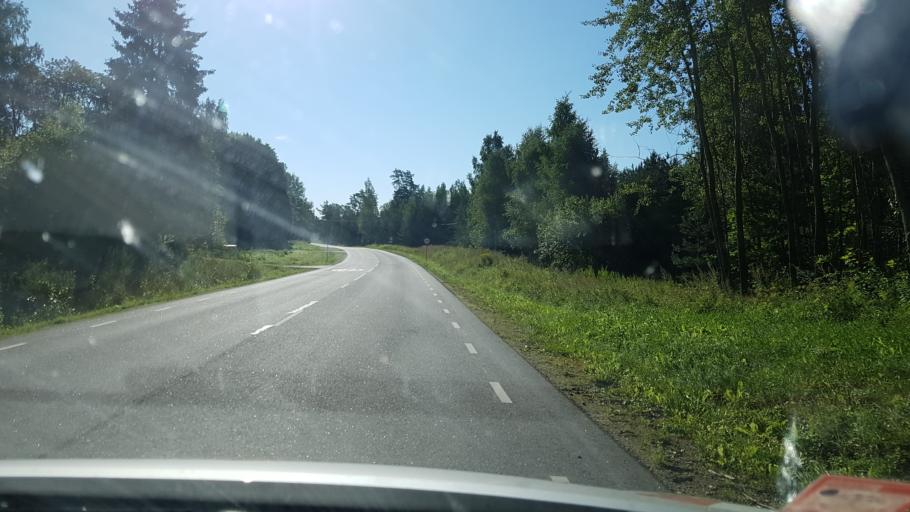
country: EE
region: Valgamaa
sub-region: Valga linn
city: Valga
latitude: 57.7566
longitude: 26.1108
